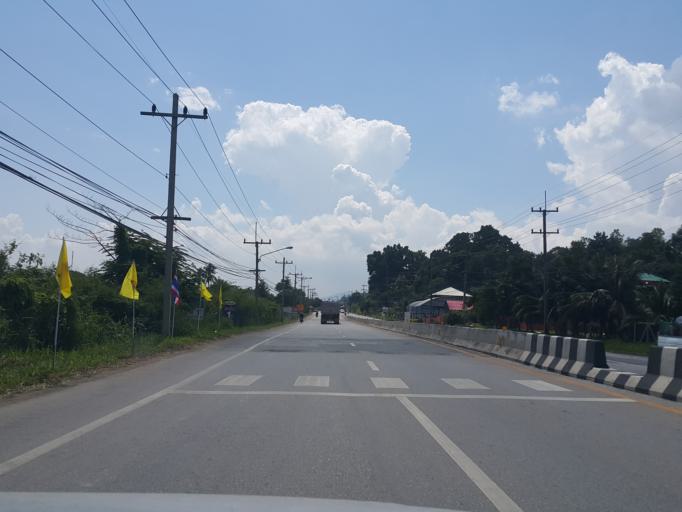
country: TH
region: Chiang Mai
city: Mae Taeng
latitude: 18.9919
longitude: 98.9458
